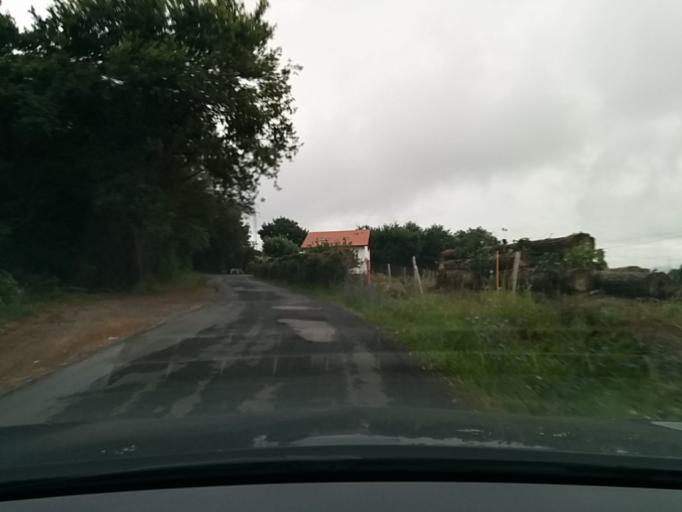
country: FR
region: Aquitaine
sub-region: Departement des Pyrenees-Atlantiques
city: Saint-Jean-de-Luz
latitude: 43.3954
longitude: -1.6368
